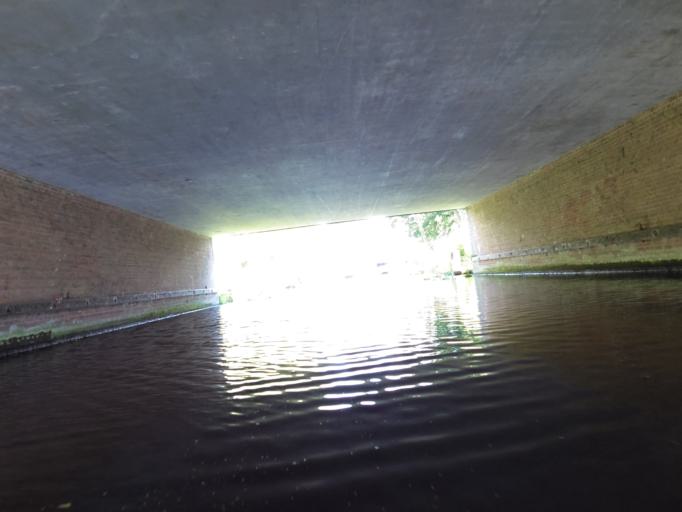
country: NL
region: South Holland
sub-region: Gemeente Wassenaar
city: Wassenaar
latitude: 52.1442
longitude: 4.4025
